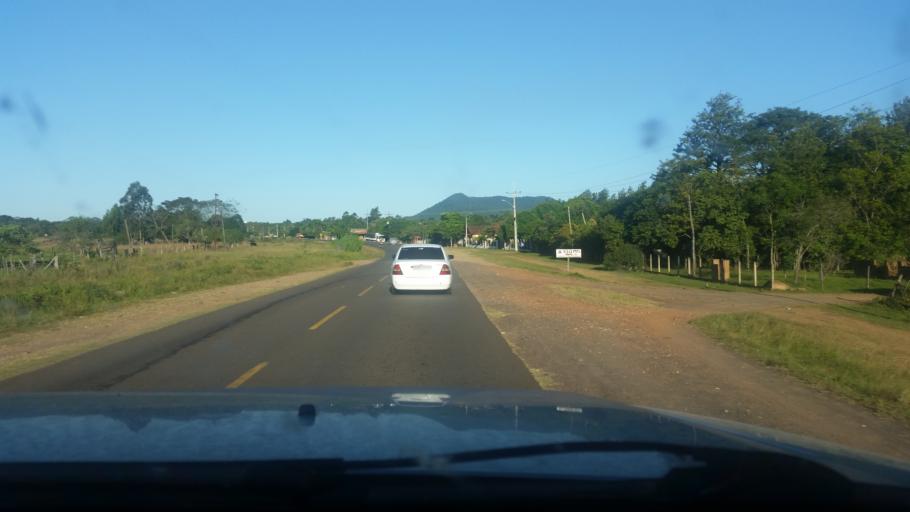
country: PY
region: Guaira
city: Mbocayaty
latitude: -25.7218
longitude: -56.3265
